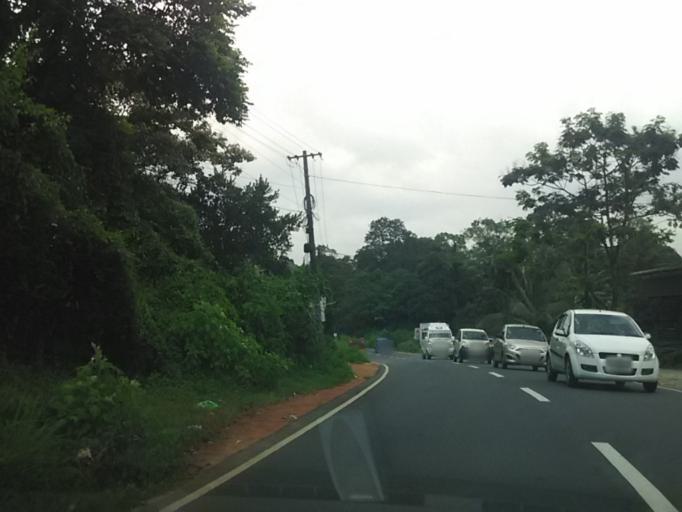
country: IN
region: Kerala
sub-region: Wayanad
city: Kalpetta
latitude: 11.5473
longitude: 76.0393
